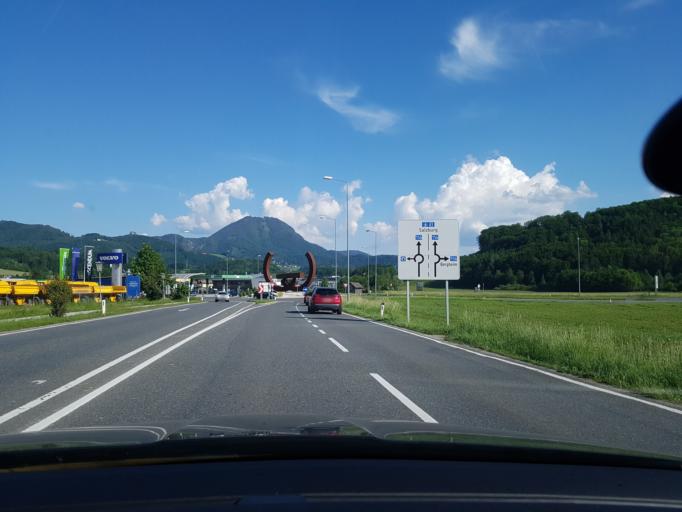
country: AT
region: Salzburg
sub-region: Politischer Bezirk Salzburg-Umgebung
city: Bergheim
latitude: 47.8450
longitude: 13.0487
